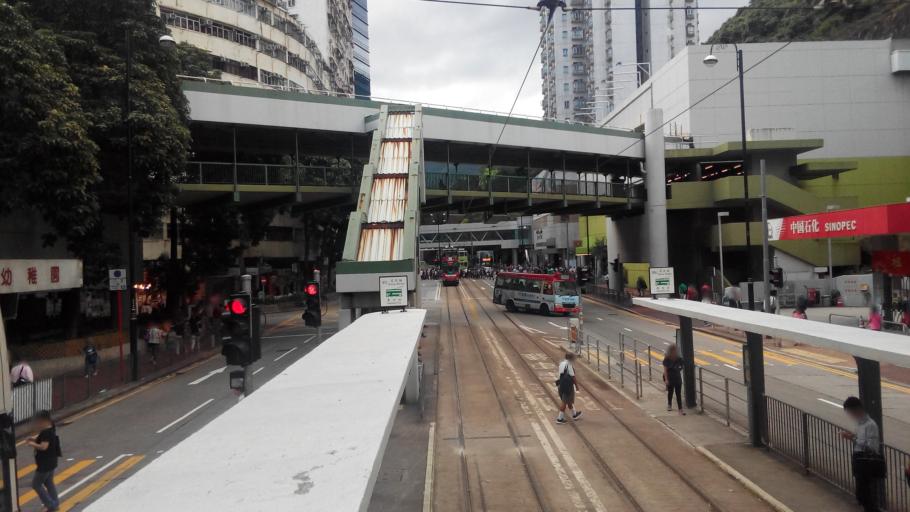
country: HK
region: Wanchai
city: Wan Chai
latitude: 22.2886
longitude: 114.2098
